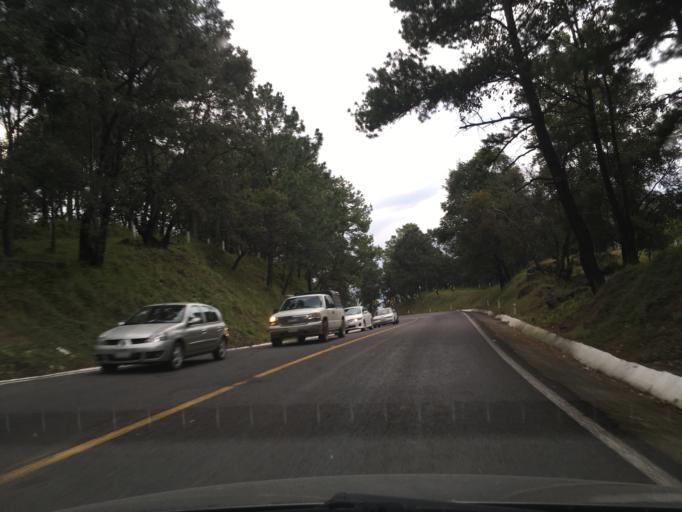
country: MX
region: Michoacan
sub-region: Patzcuaro
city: Santa Maria Huiramangaro (San Juan Tumbio)
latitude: 19.4967
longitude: -101.7113
